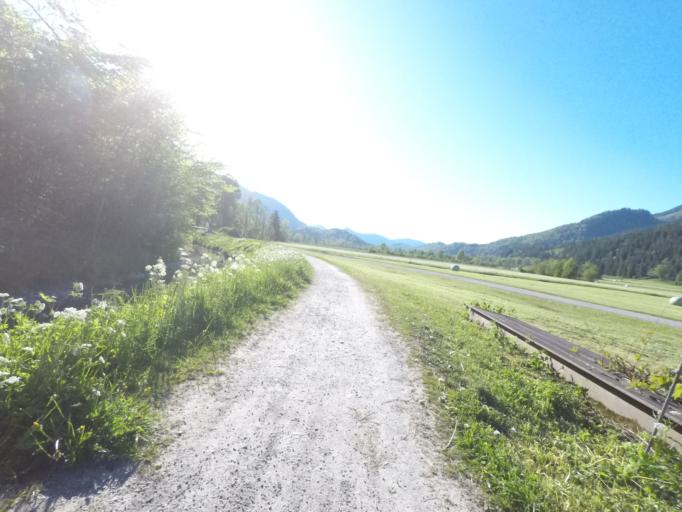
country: DE
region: Bavaria
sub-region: Upper Bavaria
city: Bayrischzell
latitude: 47.6749
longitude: 12.0015
